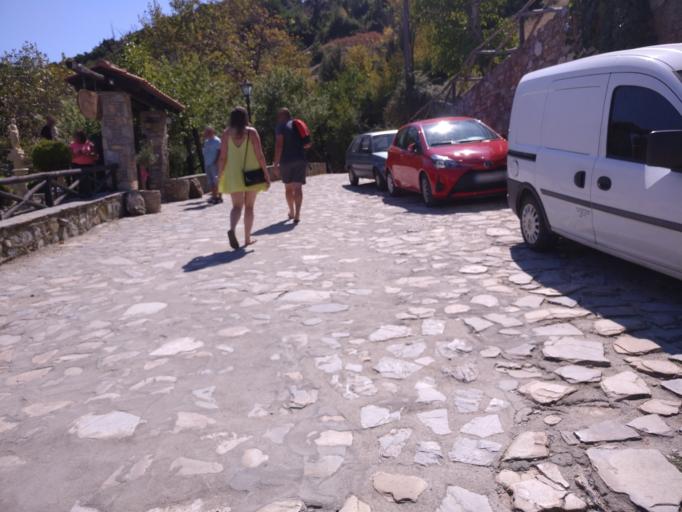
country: GR
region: Central Macedonia
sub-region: Nomos Pierias
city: Leptokarya
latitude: 39.9909
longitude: 22.5714
